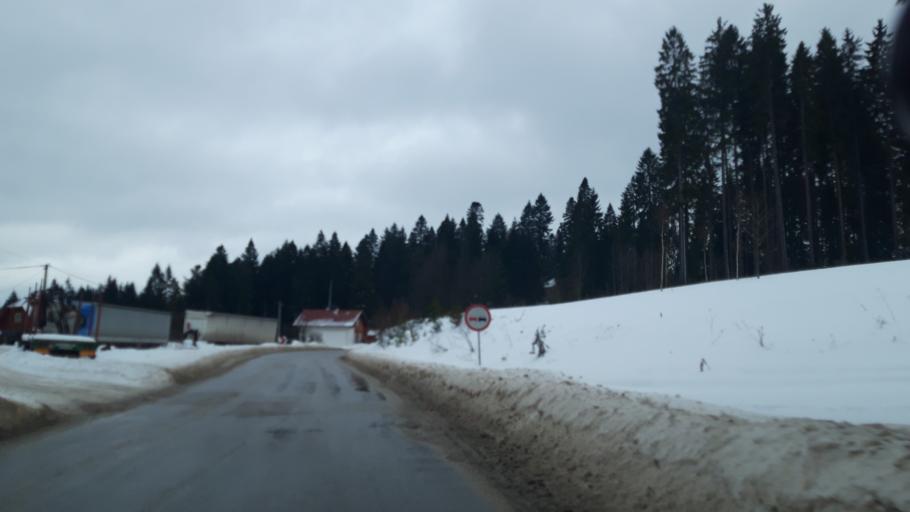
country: BA
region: Republika Srpska
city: Han Pijesak
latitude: 44.0798
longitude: 18.9523
